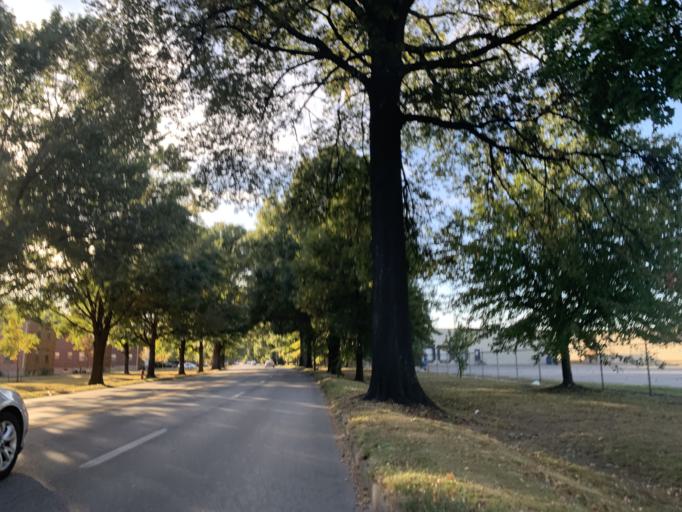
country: US
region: Kentucky
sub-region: Jefferson County
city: Louisville
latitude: 38.2225
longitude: -85.7841
